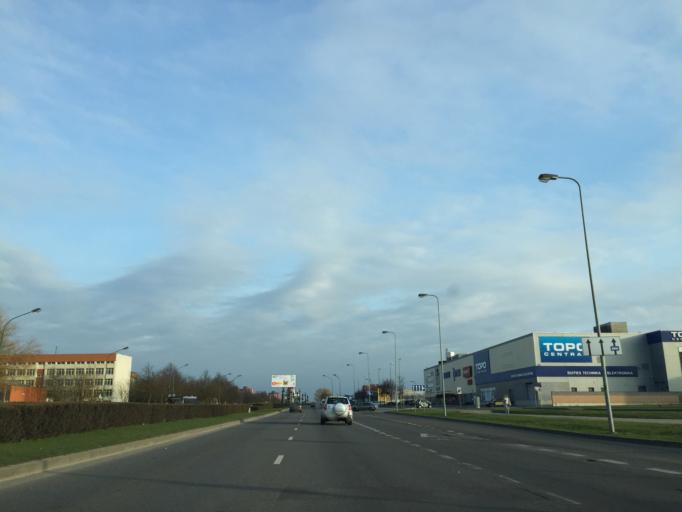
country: LT
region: Klaipedos apskritis
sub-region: Klaipeda
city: Klaipeda
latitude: 55.6888
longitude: 21.1562
